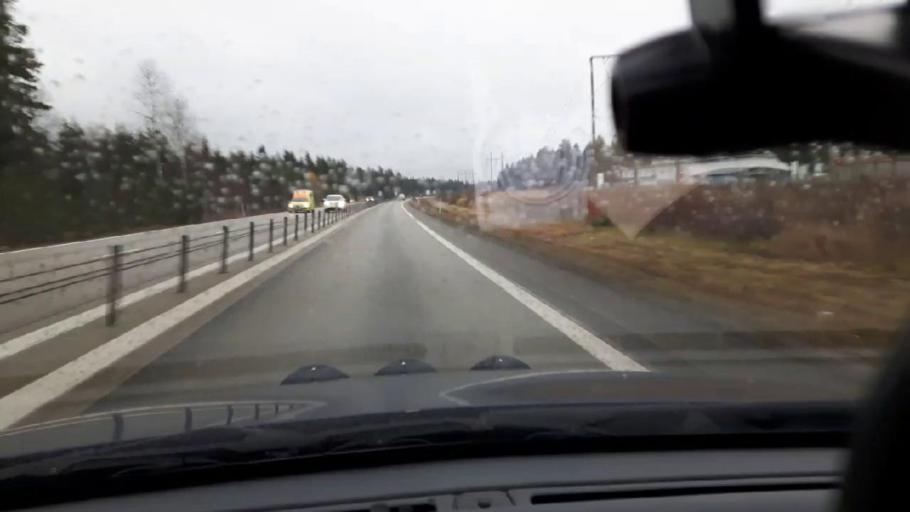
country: SE
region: Jaemtland
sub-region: OEstersunds Kommun
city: Brunflo
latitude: 63.1597
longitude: 14.7564
